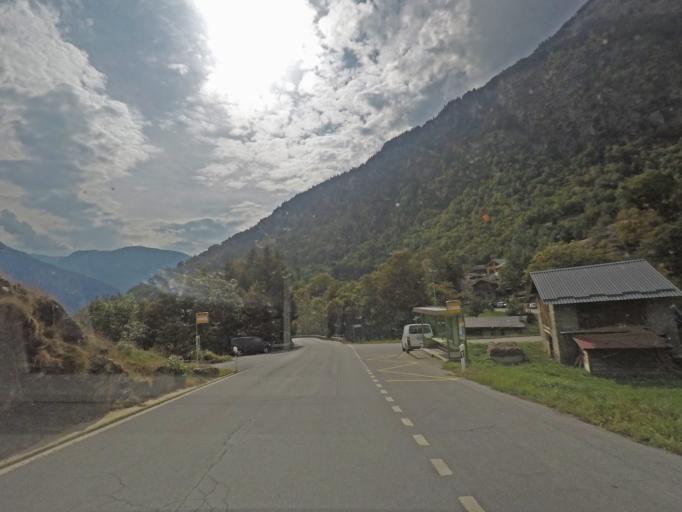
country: CH
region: Valais
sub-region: Brig District
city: Naters
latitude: 46.3356
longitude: 7.9850
